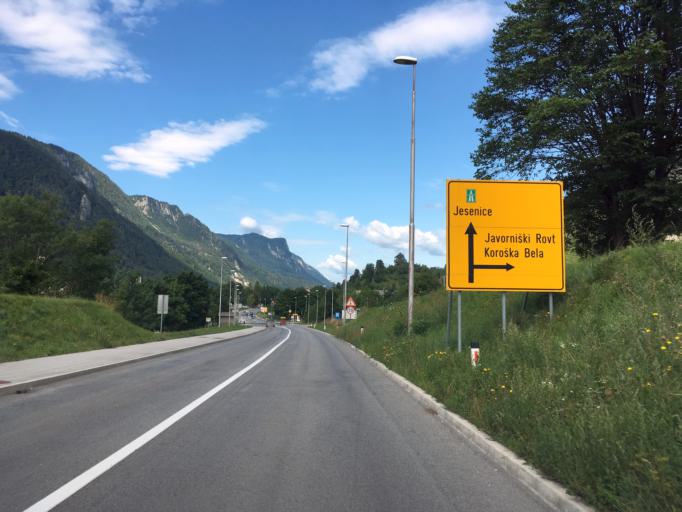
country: SI
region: Jesenice
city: Slovenski Javornik
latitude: 46.4257
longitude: 14.0953
